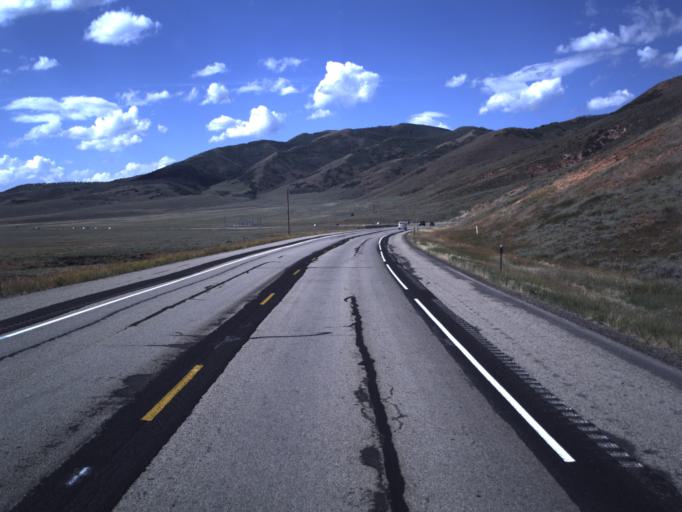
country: US
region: Utah
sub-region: Wasatch County
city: Heber
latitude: 40.2151
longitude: -111.1032
